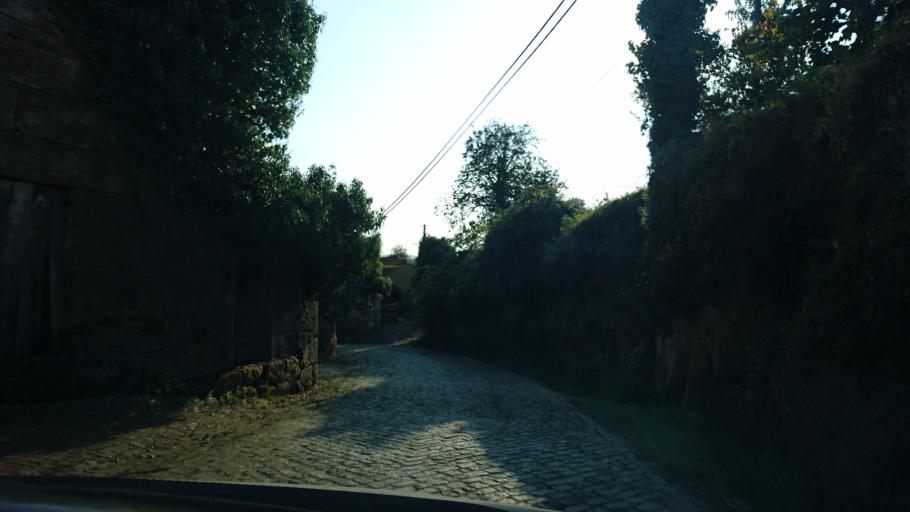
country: PT
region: Vila Real
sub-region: Mondim de Basto
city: Mondim de Basto
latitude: 41.4559
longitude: -7.9285
